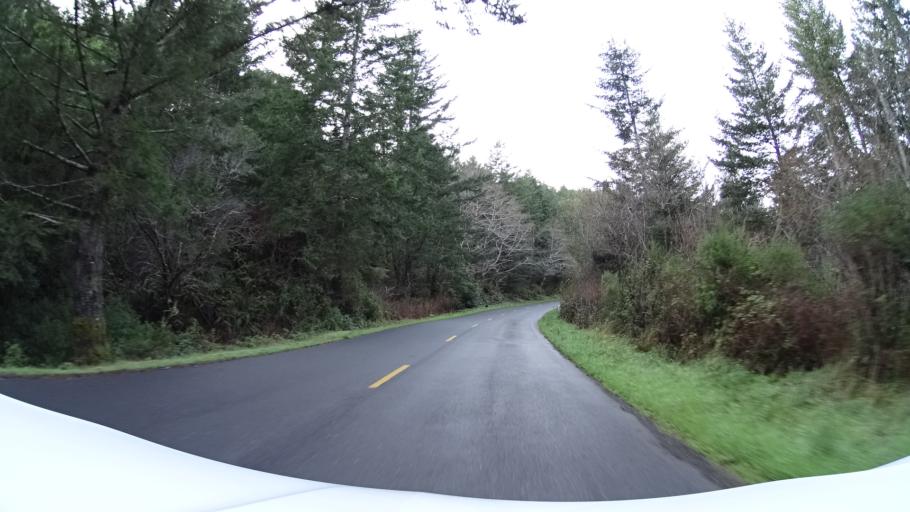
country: US
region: California
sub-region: Humboldt County
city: Ferndale
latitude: 40.3457
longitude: -124.3409
